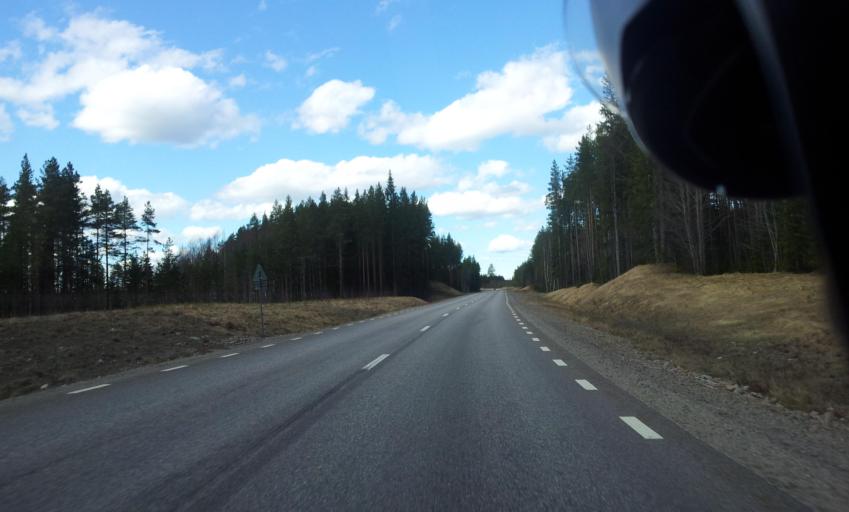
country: SE
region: Gaevleborg
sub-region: Ovanakers Kommun
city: Edsbyn
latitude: 61.1786
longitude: 15.8801
